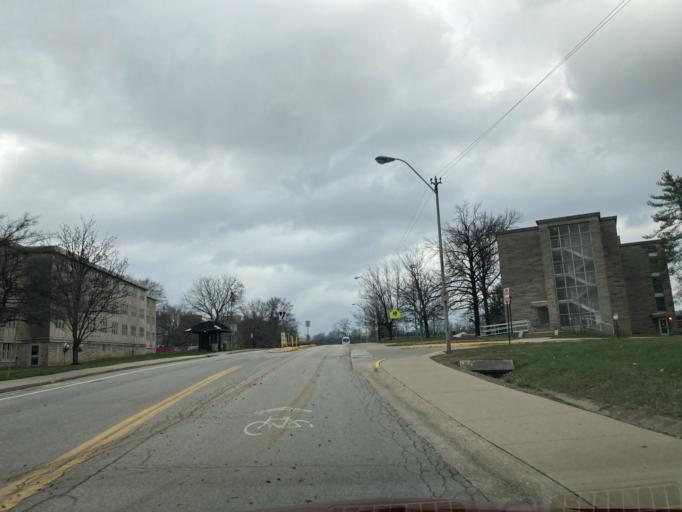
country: US
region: Indiana
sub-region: Monroe County
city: Bloomington
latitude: 39.1751
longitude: -86.5190
